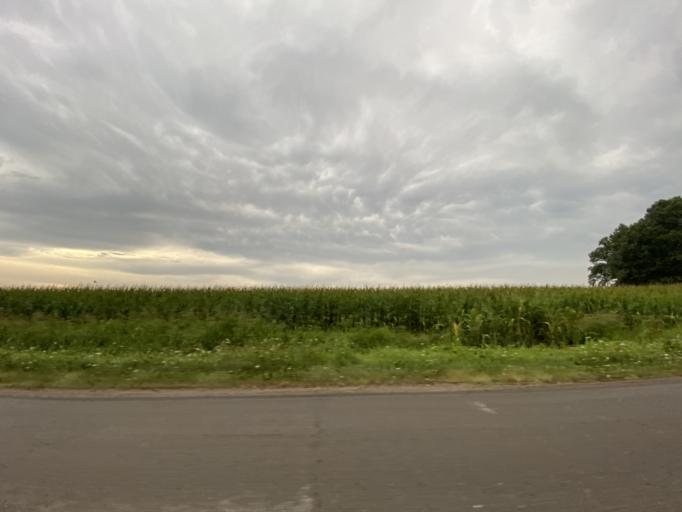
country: US
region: Alabama
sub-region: Colbert County
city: Littleville
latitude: 34.4643
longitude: -87.5079
